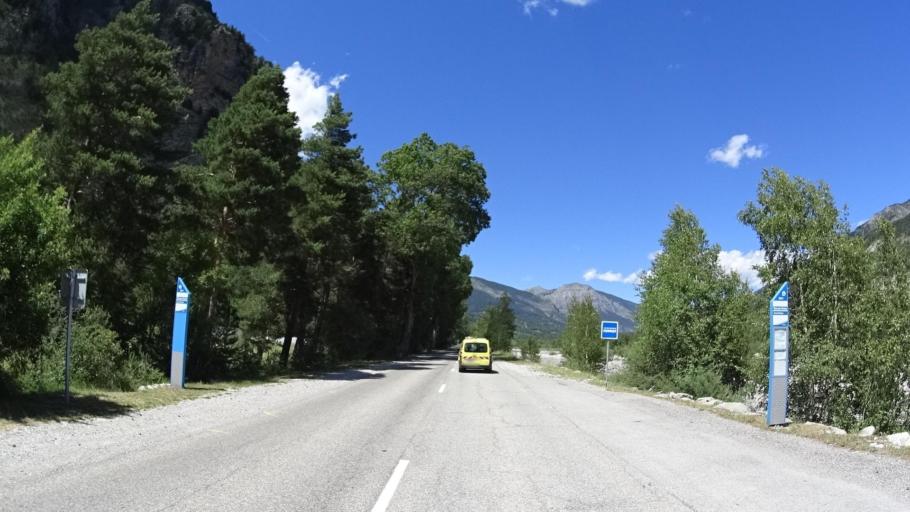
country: FR
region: Provence-Alpes-Cote d'Azur
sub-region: Departement des Alpes-de-Haute-Provence
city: Annot
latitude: 44.1129
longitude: 6.5794
